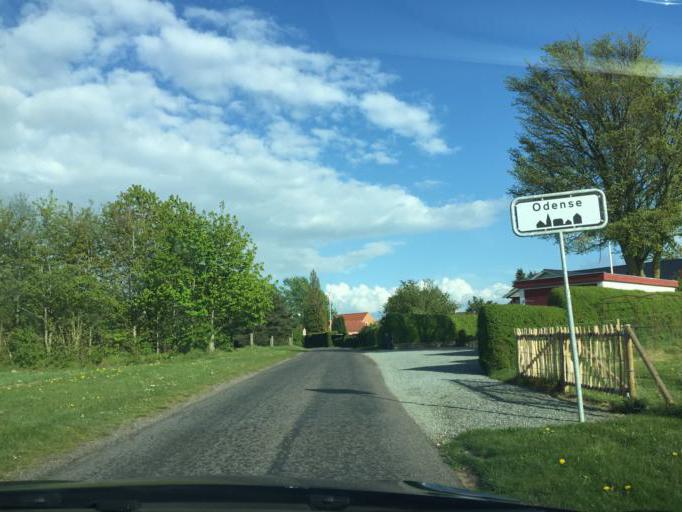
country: DK
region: South Denmark
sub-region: Odense Kommune
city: Bellinge
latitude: 55.3581
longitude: 10.3085
